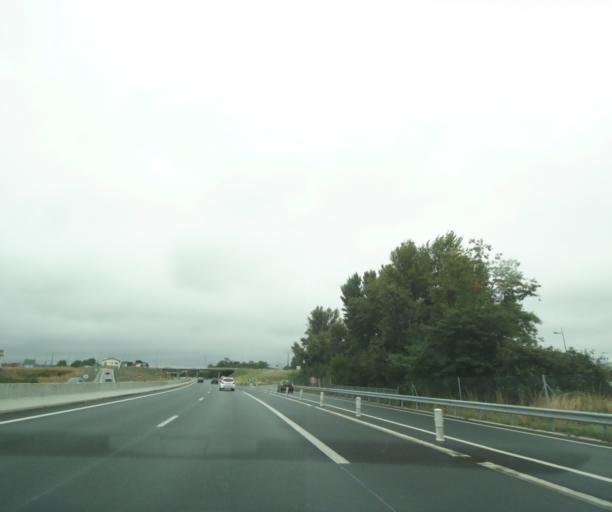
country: FR
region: Midi-Pyrenees
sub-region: Departement du Tarn
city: Albi
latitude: 43.9291
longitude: 2.1739
